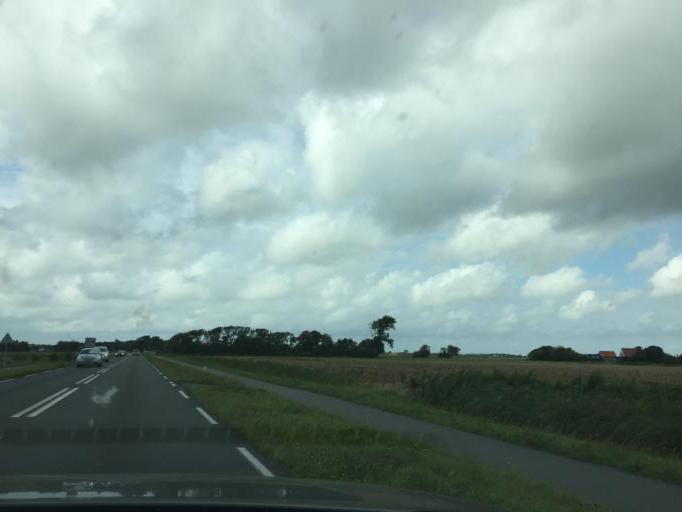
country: NL
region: North Holland
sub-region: Gemeente Texel
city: Den Burg
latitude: 53.0657
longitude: 4.7755
